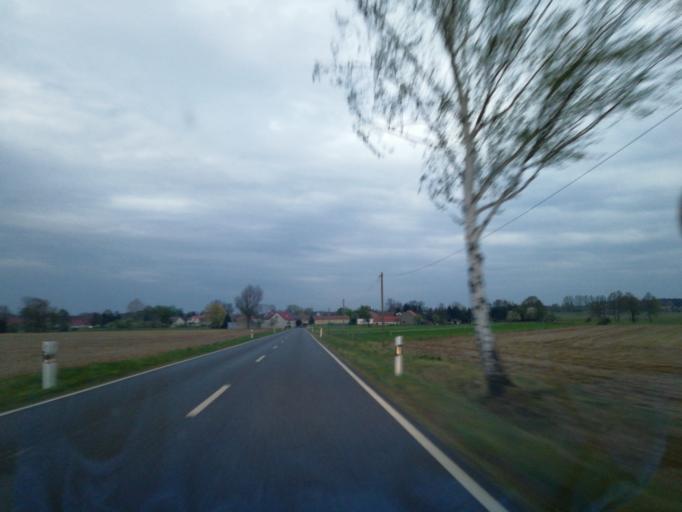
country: DE
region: Brandenburg
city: Calau
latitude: 51.7646
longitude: 13.9065
